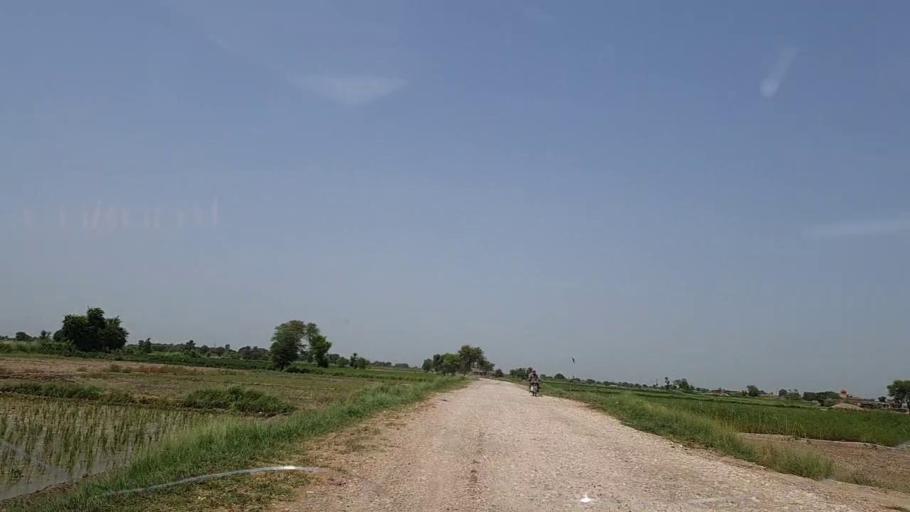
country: PK
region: Sindh
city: Tharu Shah
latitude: 26.9192
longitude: 68.0587
